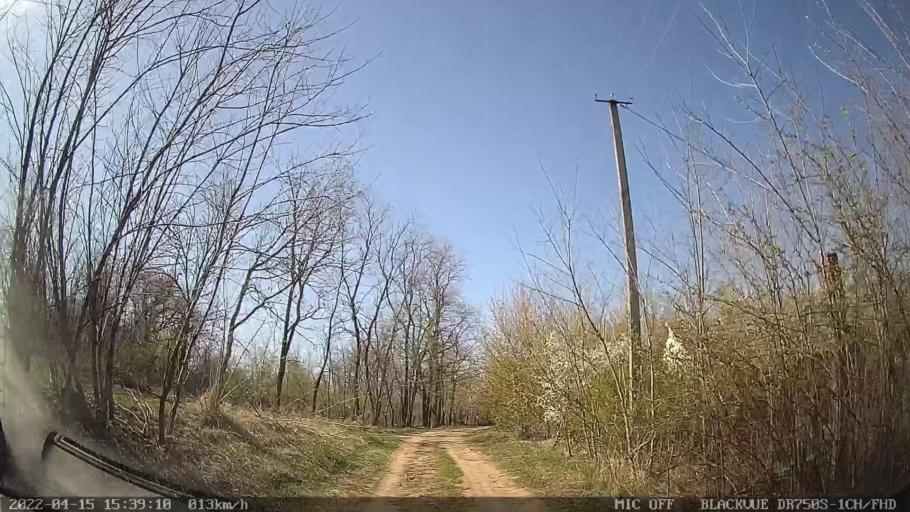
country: MD
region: Raionul Ocnita
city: Otaci
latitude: 48.3531
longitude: 27.9278
